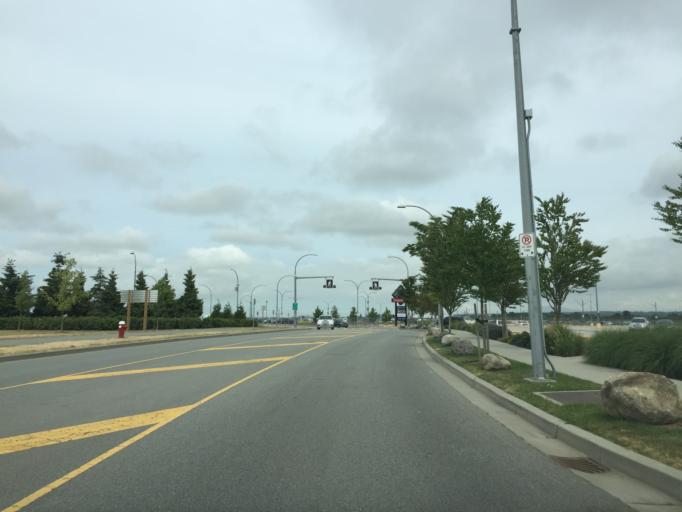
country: CA
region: British Columbia
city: Richmond
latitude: 49.1970
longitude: -123.1435
